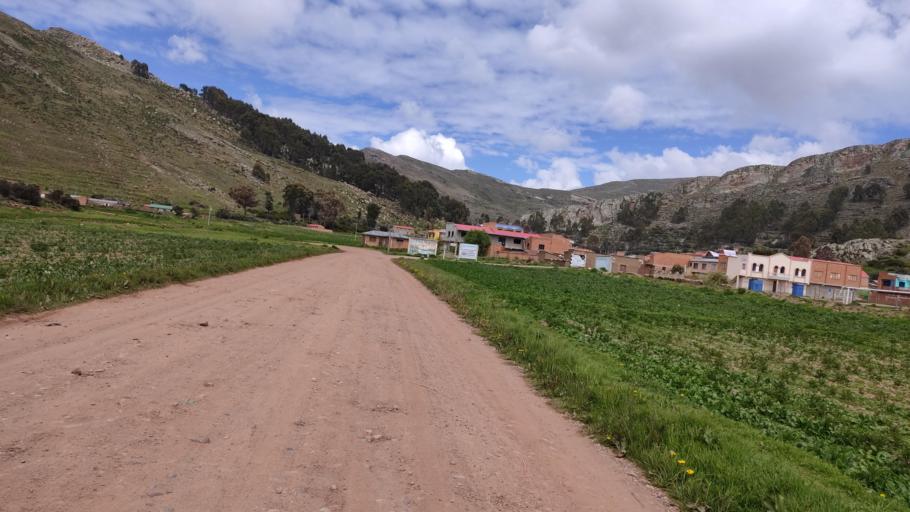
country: BO
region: La Paz
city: Batallas
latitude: -16.3494
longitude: -68.6339
